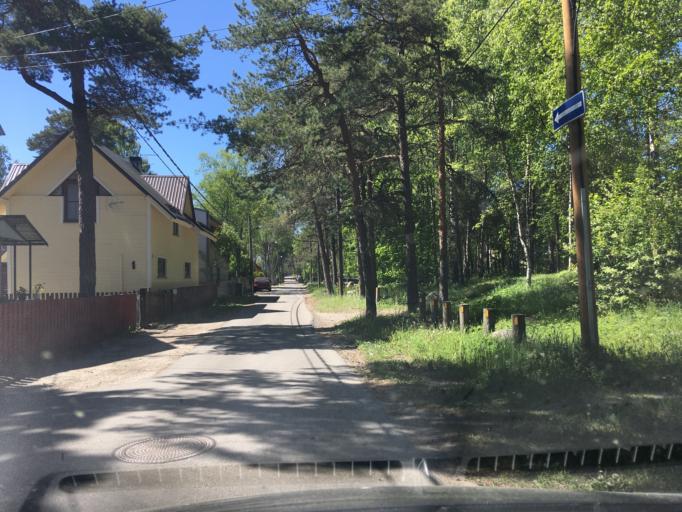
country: EE
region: Harju
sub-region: Saue vald
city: Laagri
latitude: 59.3879
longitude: 24.6735
